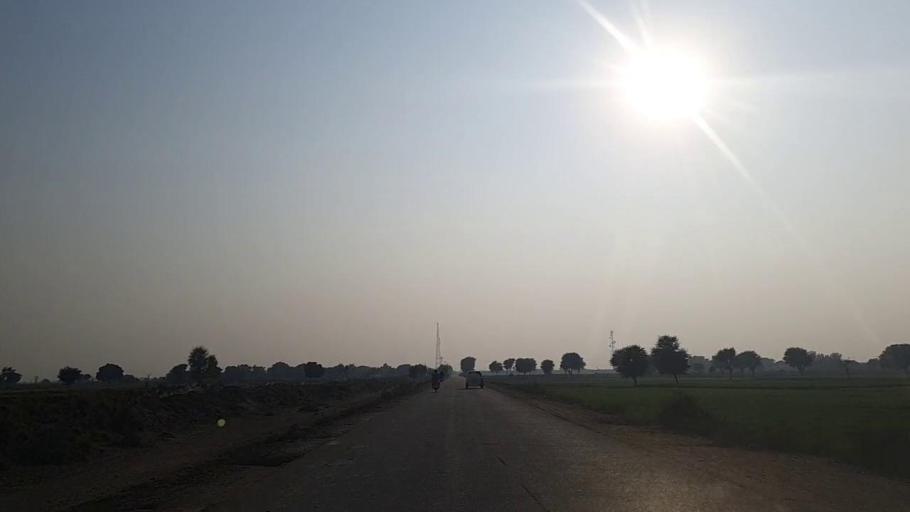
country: PK
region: Sindh
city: Shahpur Chakar
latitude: 26.2052
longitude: 68.5604
